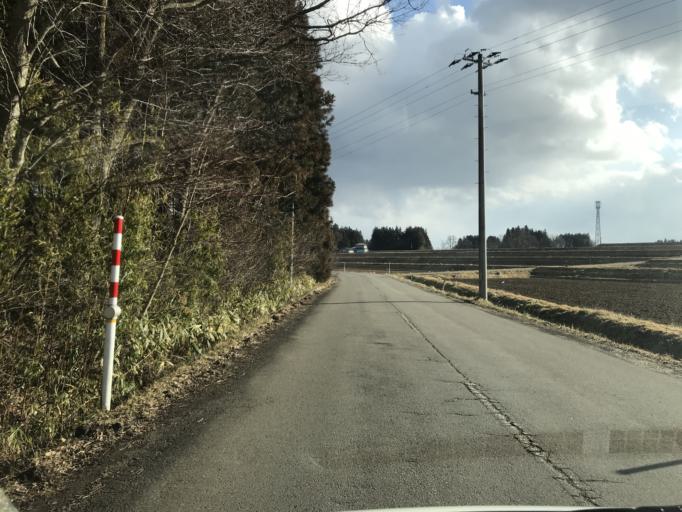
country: JP
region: Iwate
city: Mizusawa
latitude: 39.0963
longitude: 141.0351
